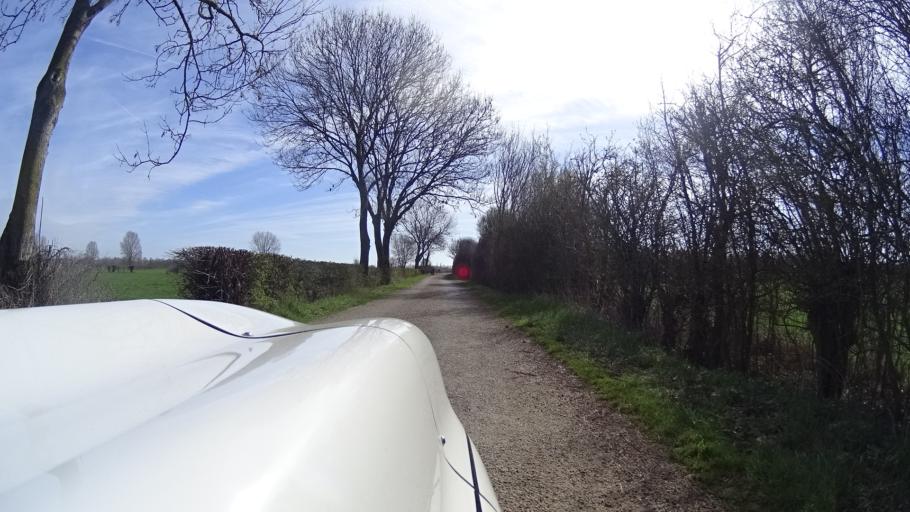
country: NL
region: Limburg
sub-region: Gemeente Gennep
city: Gennep
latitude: 51.7030
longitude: 5.9507
